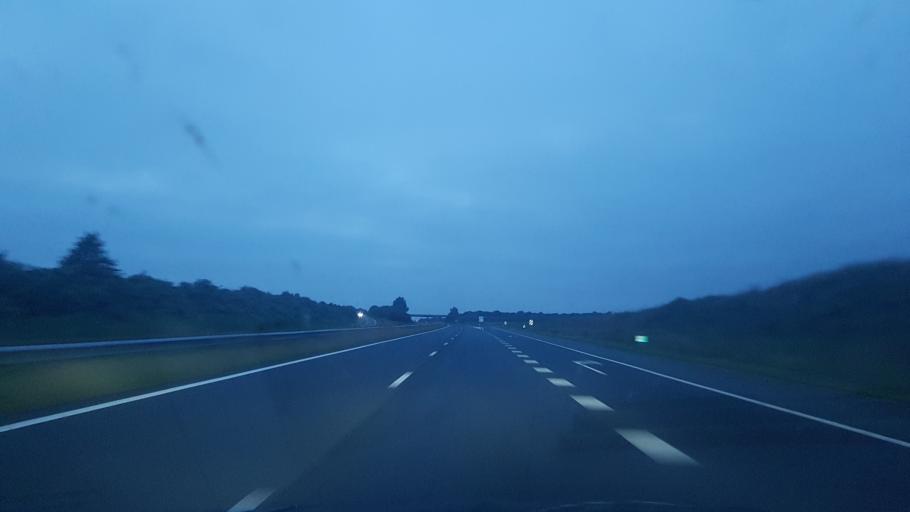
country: NL
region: Friesland
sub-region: Gemeente Boarnsterhim
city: Grou
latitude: 53.1064
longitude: 5.8156
